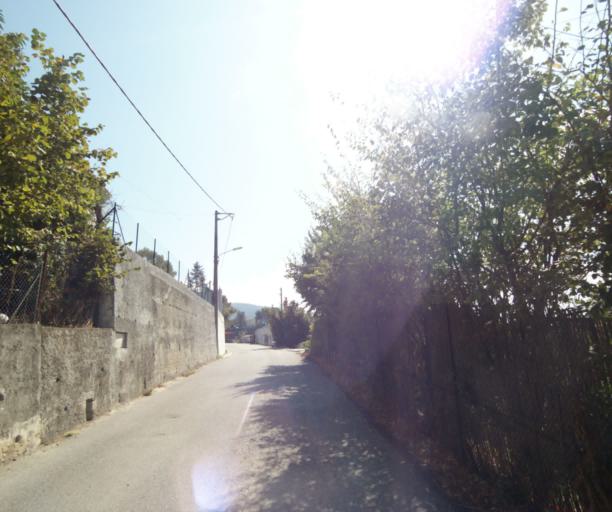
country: FR
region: Provence-Alpes-Cote d'Azur
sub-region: Departement des Alpes-Maritimes
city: Drap
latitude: 43.7541
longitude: 7.3236
